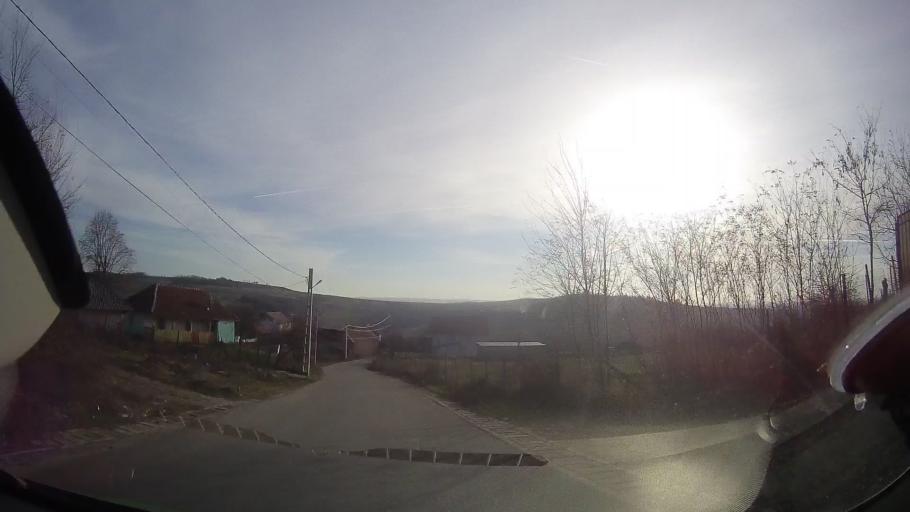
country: RO
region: Bihor
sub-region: Comuna Sarbi
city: Burzuc
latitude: 47.1113
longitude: 22.1776
